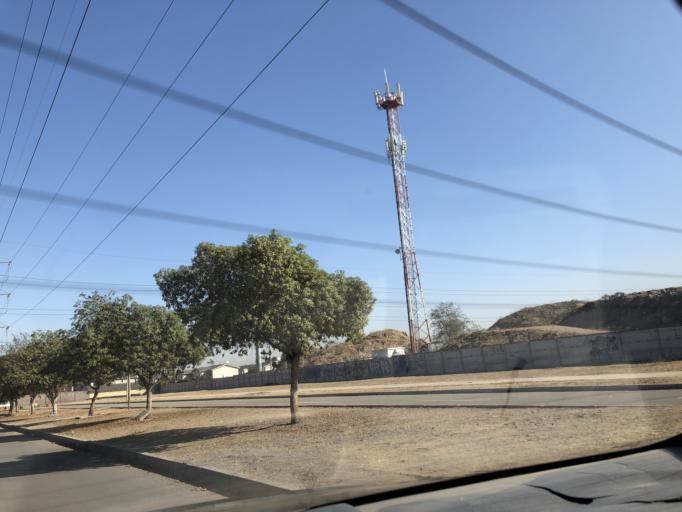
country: CL
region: Santiago Metropolitan
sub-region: Provincia de Santiago
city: La Pintana
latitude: -33.5750
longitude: -70.5958
